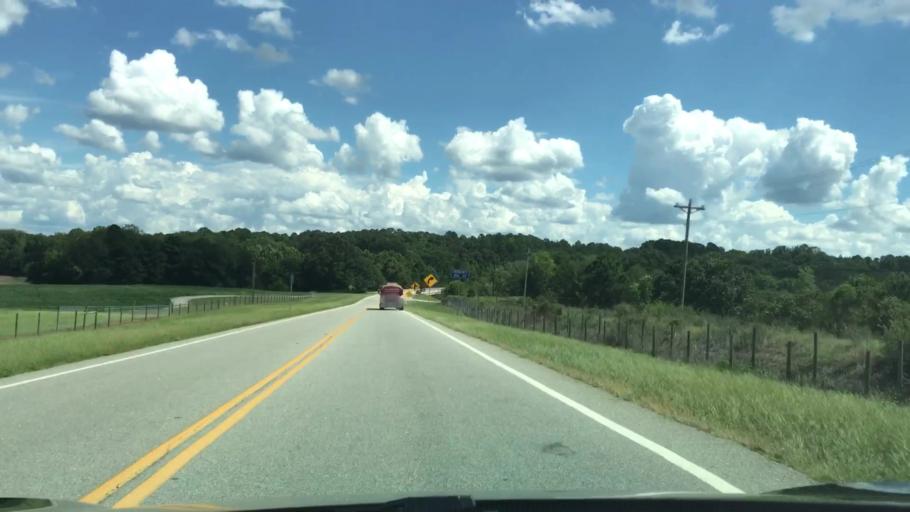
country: US
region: Georgia
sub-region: Oconee County
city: Watkinsville
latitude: 33.7224
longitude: -83.2994
